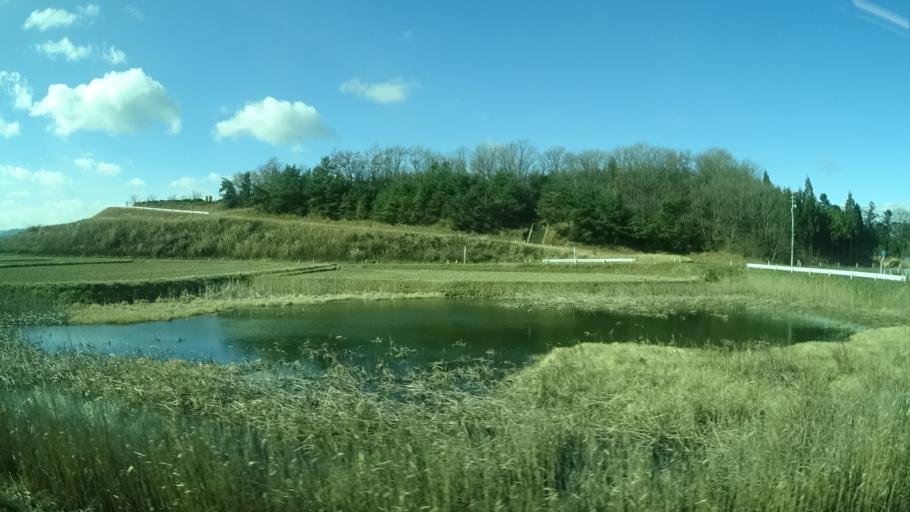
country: JP
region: Miyagi
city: Marumori
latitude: 37.8616
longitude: 140.9294
